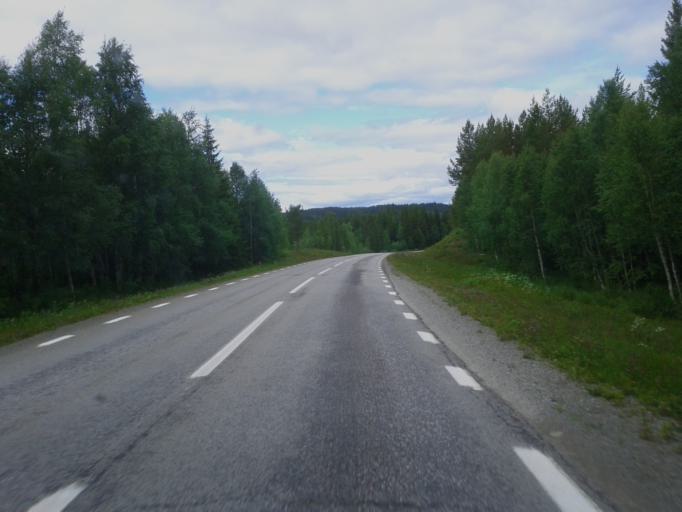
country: SE
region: Vaesterbotten
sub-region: Storumans Kommun
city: Fristad
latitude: 65.3599
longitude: 16.5383
